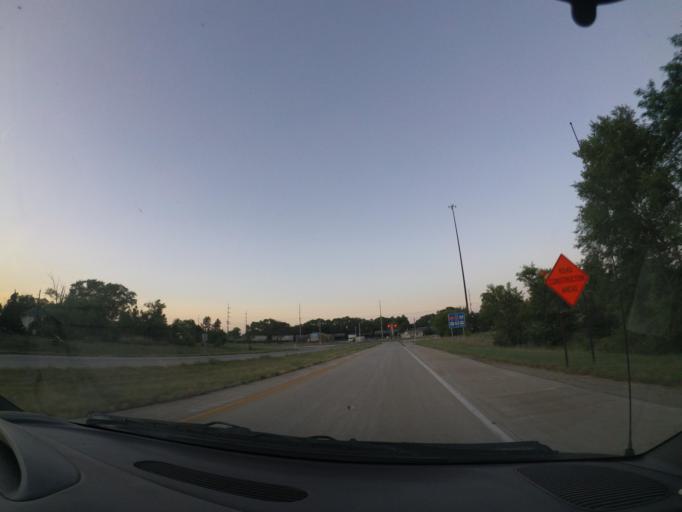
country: US
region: Indiana
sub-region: Elkhart County
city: Dunlap
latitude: 41.6526
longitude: -85.9436
